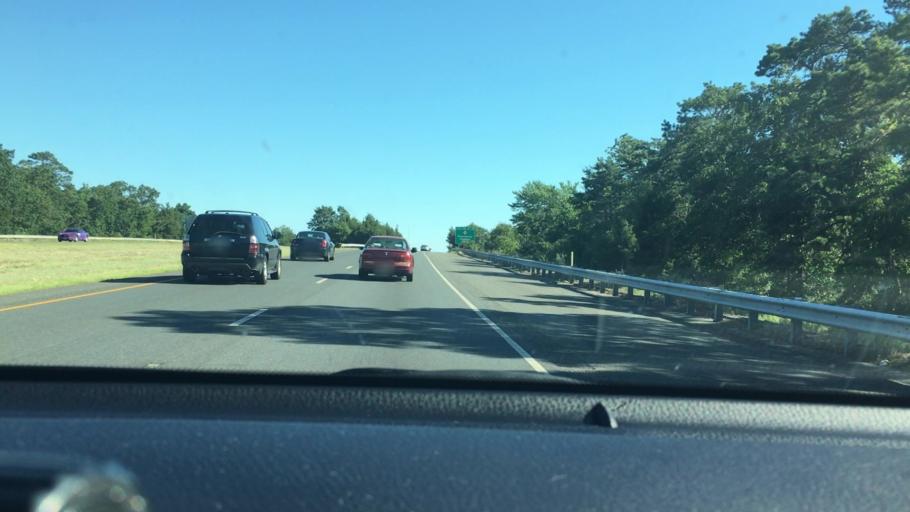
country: US
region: New Jersey
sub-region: Cumberland County
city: Vineland
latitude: 39.5071
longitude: -75.0696
